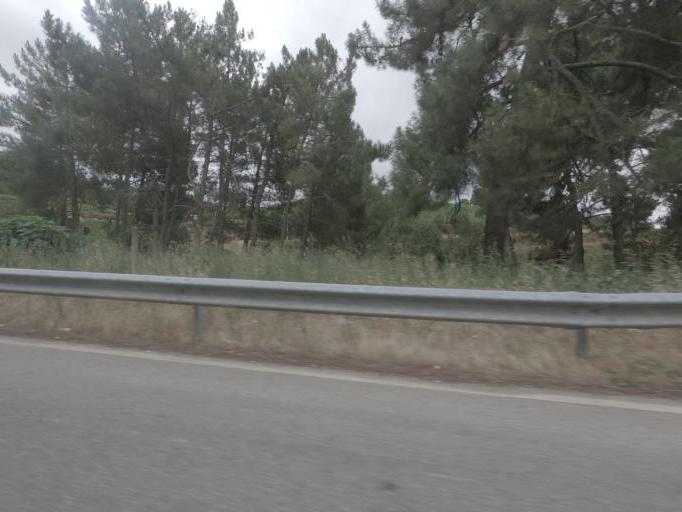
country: PT
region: Vila Real
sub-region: Sabrosa
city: Sabrosa
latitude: 41.2845
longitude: -7.5100
